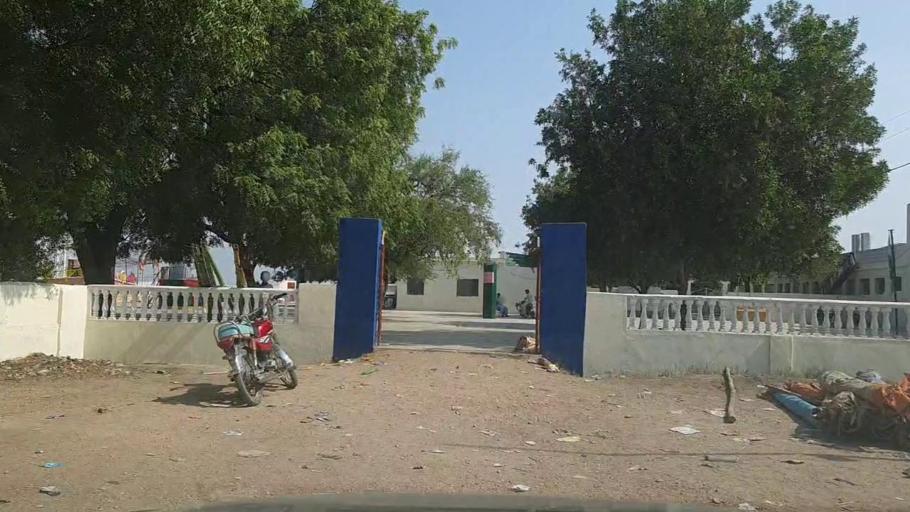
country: PK
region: Sindh
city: Thatta
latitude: 24.6234
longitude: 67.9660
